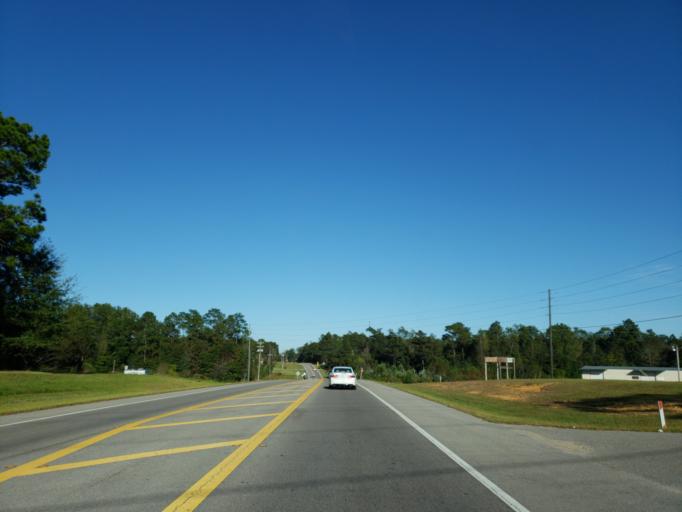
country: US
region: Mississippi
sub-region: Forrest County
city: Petal
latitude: 31.3523
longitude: -89.1731
